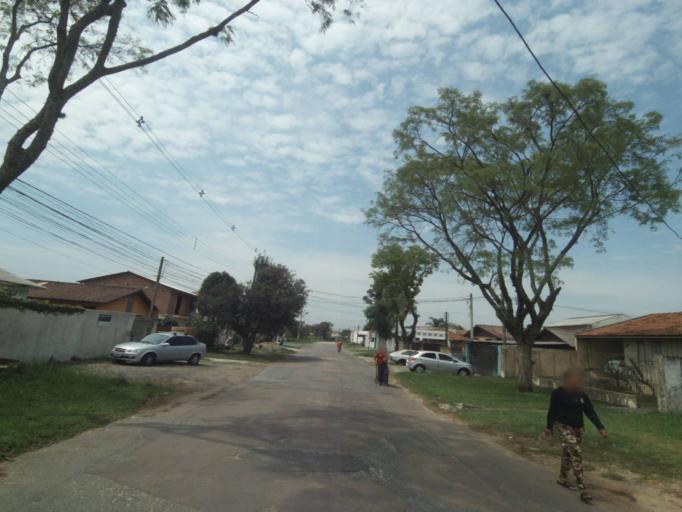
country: BR
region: Parana
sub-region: Pinhais
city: Pinhais
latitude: -25.4228
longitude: -49.1989
